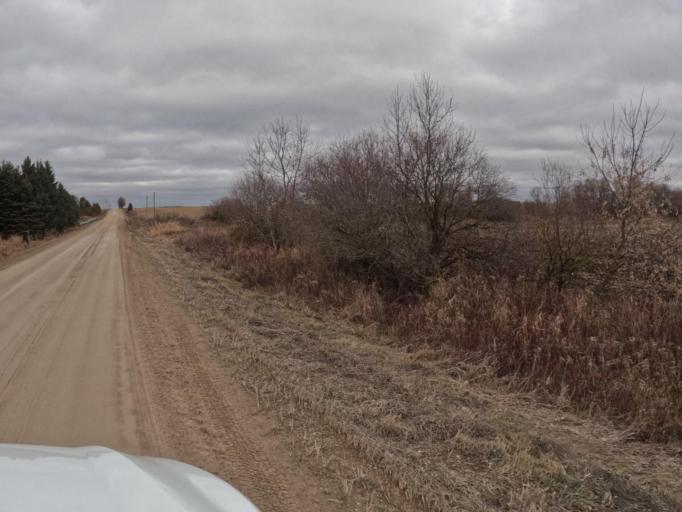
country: CA
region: Ontario
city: Shelburne
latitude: 43.8763
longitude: -80.3795
